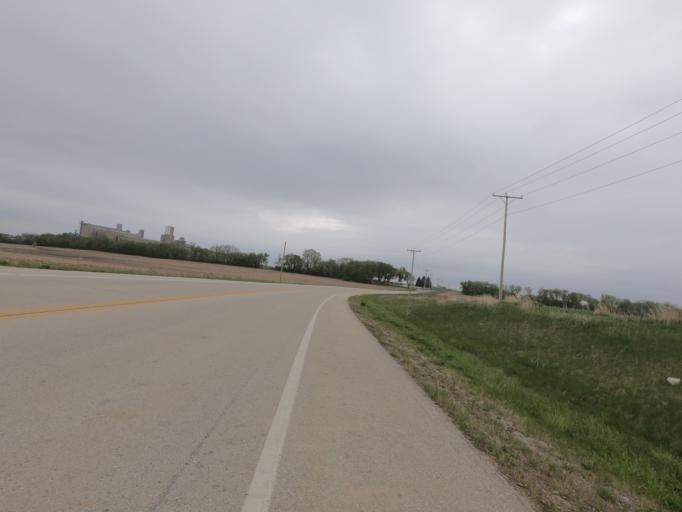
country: US
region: Wisconsin
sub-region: Jefferson County
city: Jefferson
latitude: 43.0317
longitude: -88.8009
